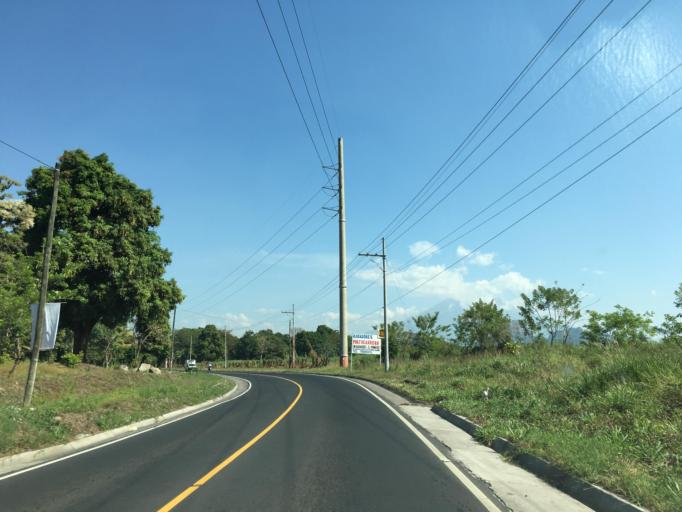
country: GT
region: Escuintla
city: Siquinala
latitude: 14.2880
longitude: -90.9690
